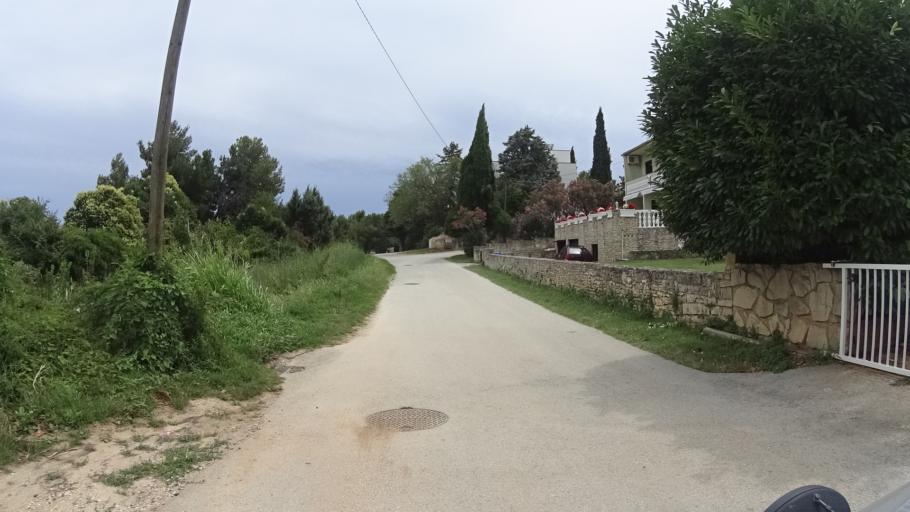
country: HR
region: Istarska
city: Medulin
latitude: 44.8012
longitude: 13.9145
